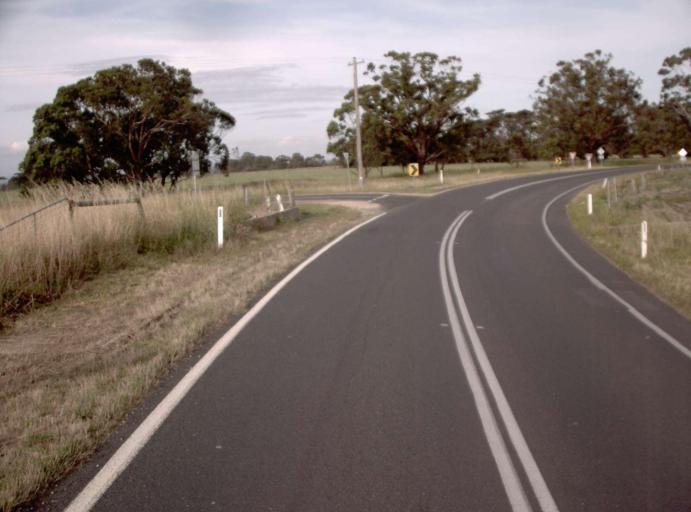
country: AU
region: Victoria
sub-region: Wellington
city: Heyfield
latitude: -38.0124
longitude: 146.6722
